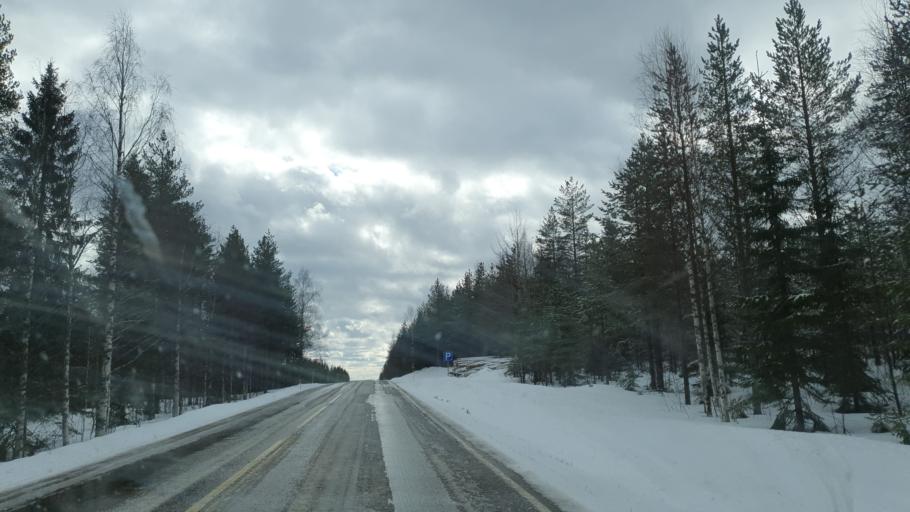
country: FI
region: Kainuu
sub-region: Kehys-Kainuu
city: Puolanka
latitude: 64.9540
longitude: 27.6007
